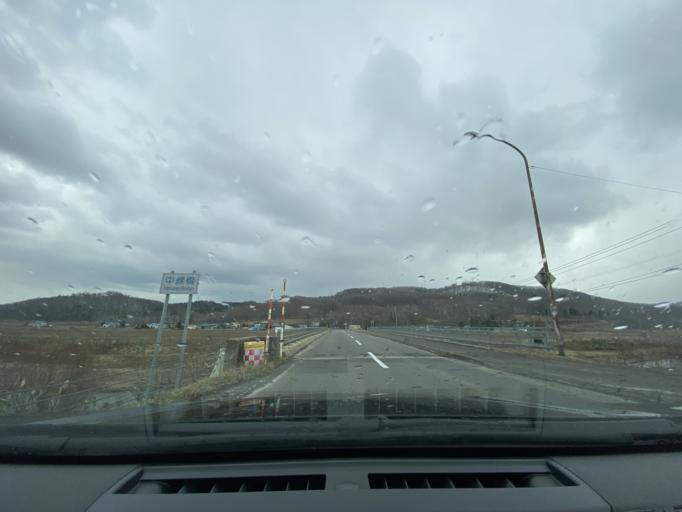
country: JP
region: Hokkaido
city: Nayoro
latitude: 44.1702
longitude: 142.2668
